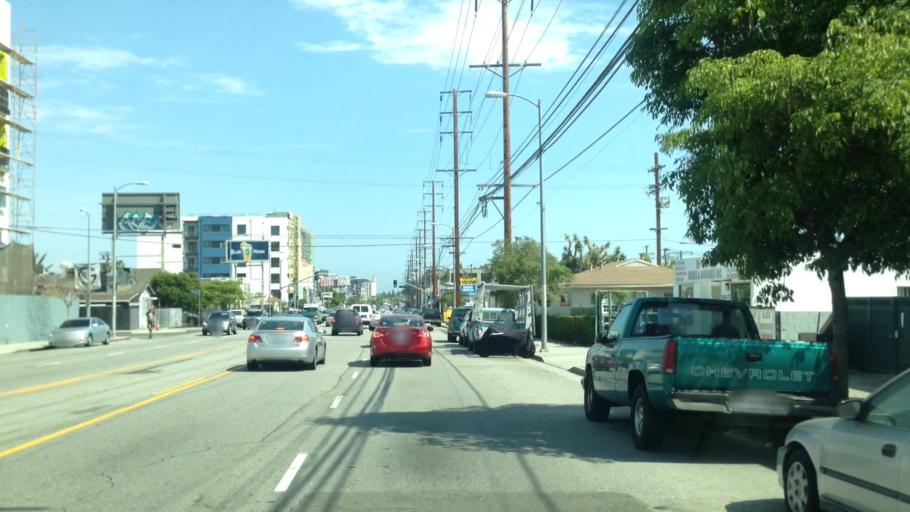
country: US
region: California
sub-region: Los Angeles County
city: Culver City
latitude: 34.0238
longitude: -118.4110
